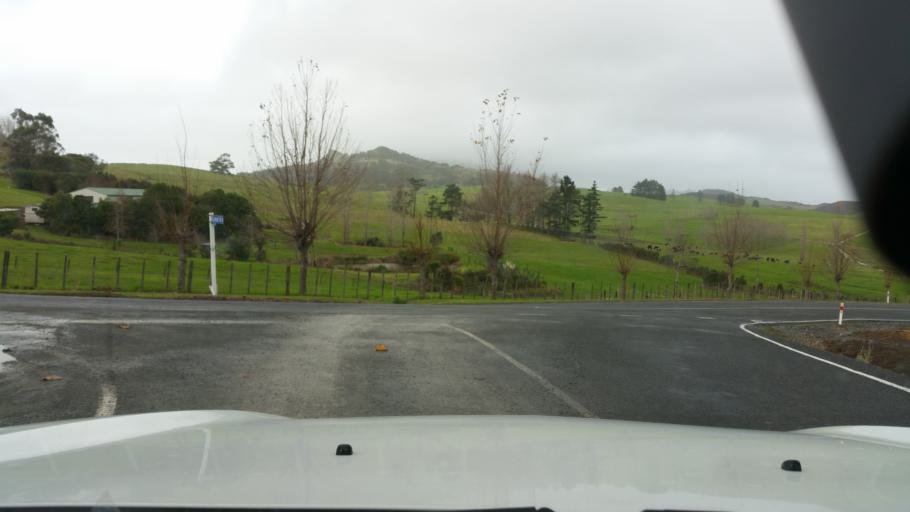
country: NZ
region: Northland
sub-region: Whangarei
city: Ngunguru
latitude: -35.7631
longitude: 174.4947
